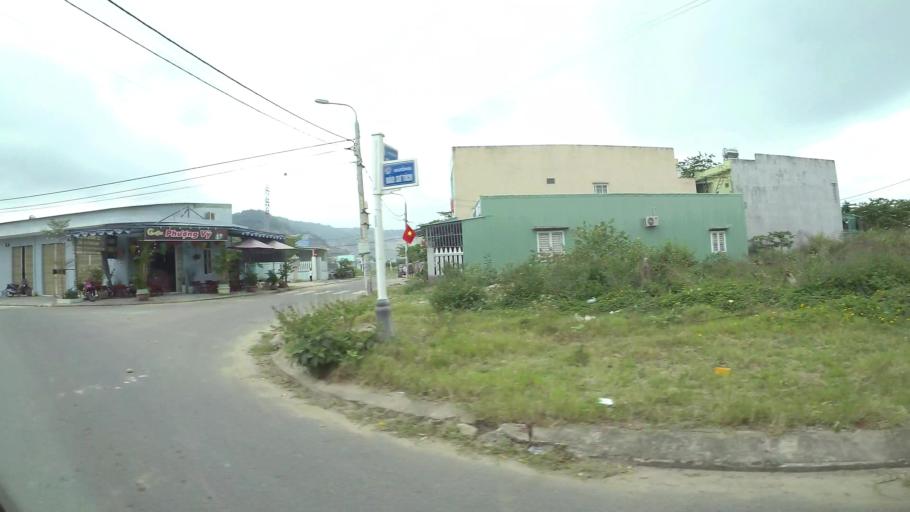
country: VN
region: Da Nang
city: Lien Chieu
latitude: 16.0512
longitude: 108.1675
